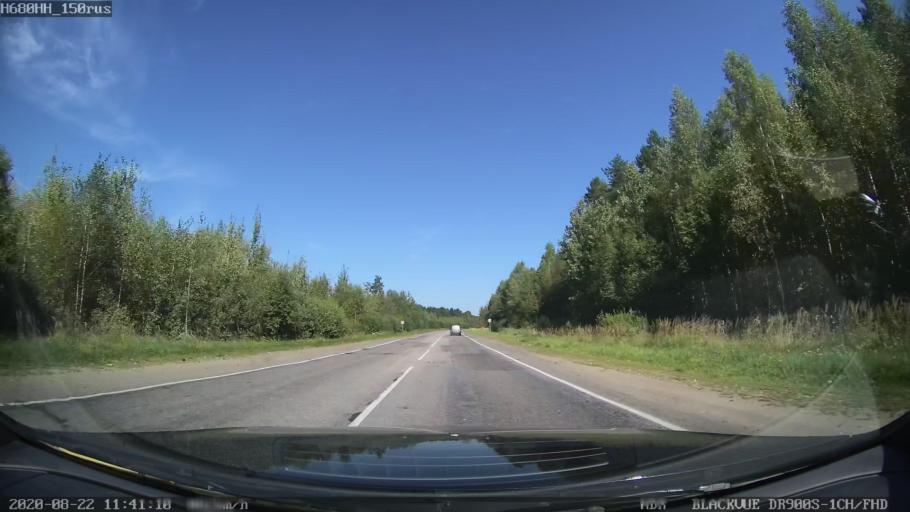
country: RU
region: Tverskaya
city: Sakharovo
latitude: 56.9861
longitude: 36.0237
